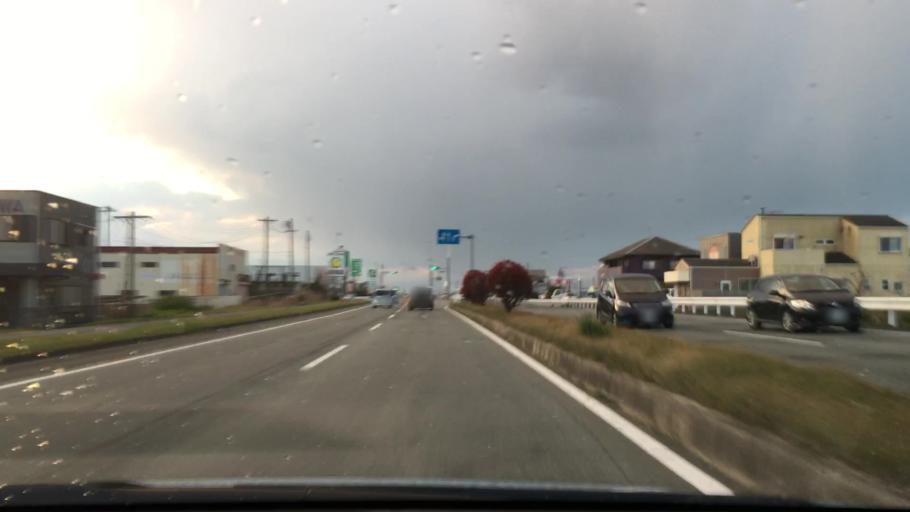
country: JP
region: Mie
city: Ise
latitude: 34.5357
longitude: 136.6770
